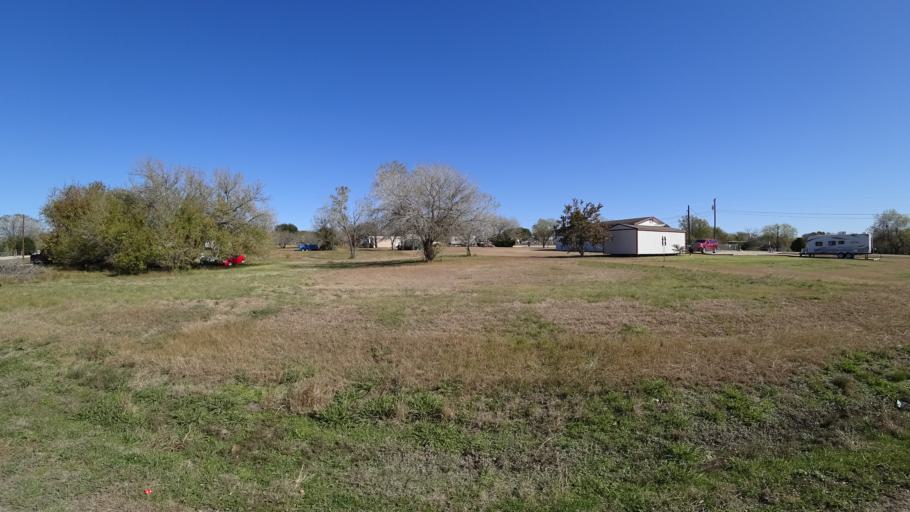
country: US
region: Texas
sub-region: Travis County
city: Garfield
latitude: 30.1040
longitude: -97.5973
